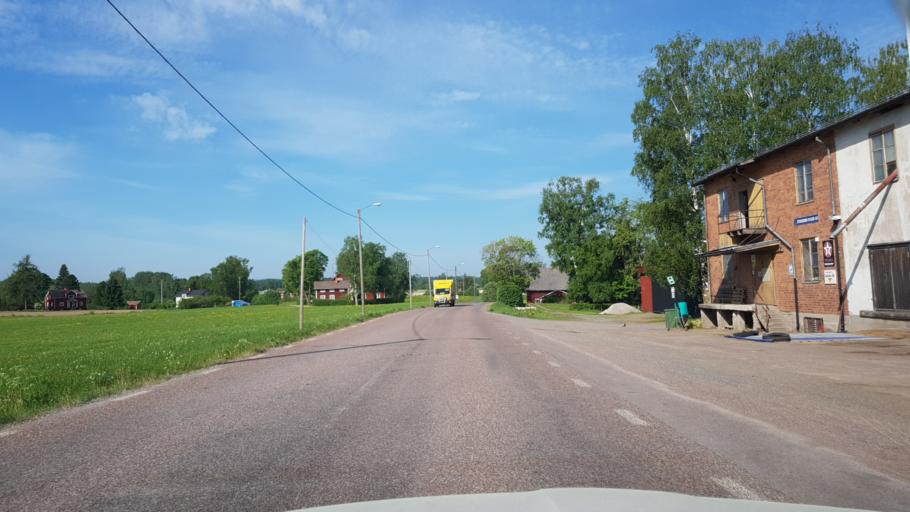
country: SE
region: Dalarna
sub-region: Saters Kommun
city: Saeter
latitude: 60.4169
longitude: 15.7420
